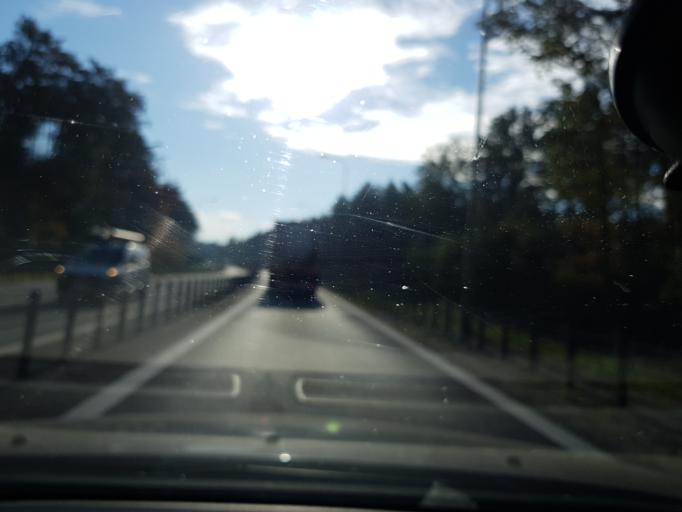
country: PL
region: Masovian Voivodeship
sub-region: Powiat zyrardowski
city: Zyrardow
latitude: 52.0345
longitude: 20.4212
